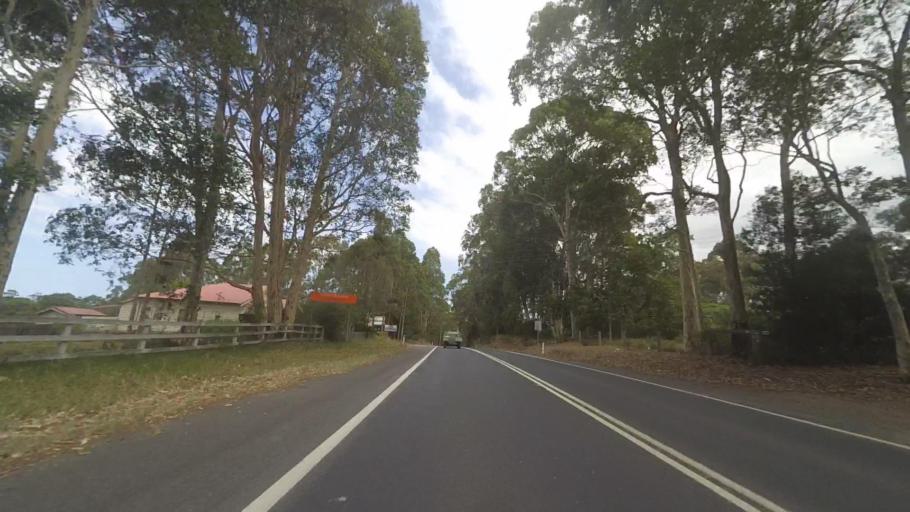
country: AU
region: New South Wales
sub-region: Shoalhaven Shire
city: Falls Creek
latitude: -35.0831
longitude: 150.5174
